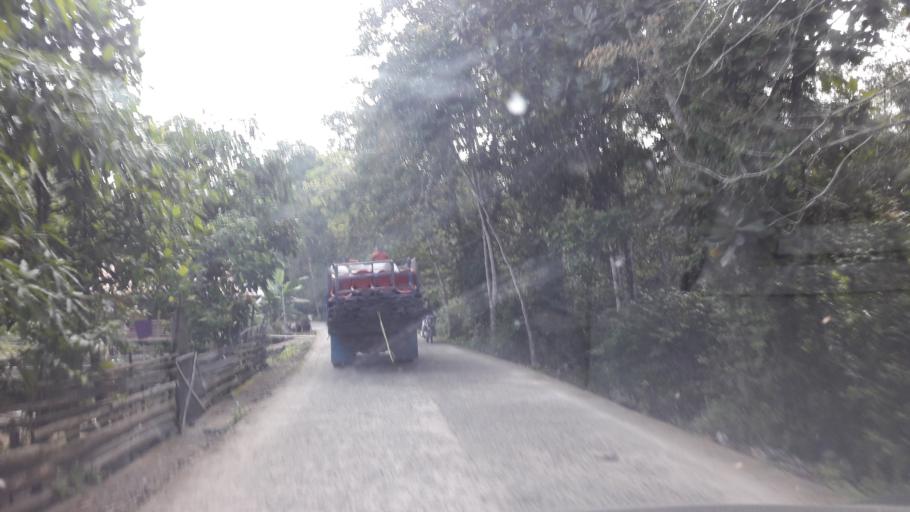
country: ID
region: South Sumatra
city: Gunungmenang
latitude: -3.1079
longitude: 103.9586
